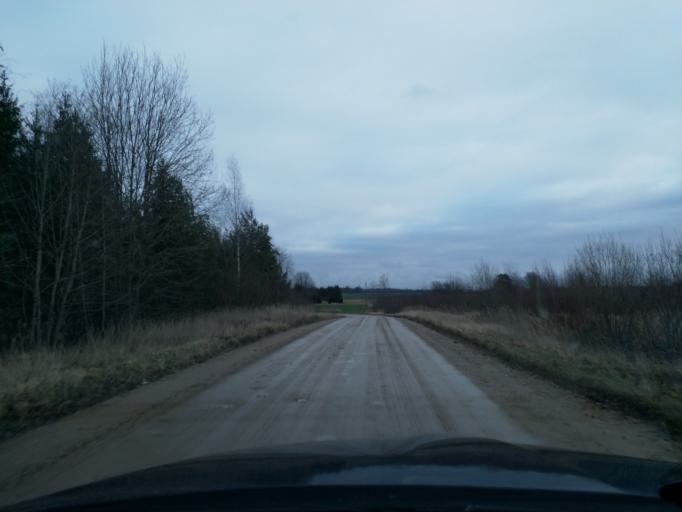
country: LV
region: Saldus Rajons
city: Saldus
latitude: 56.8939
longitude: 22.2938
